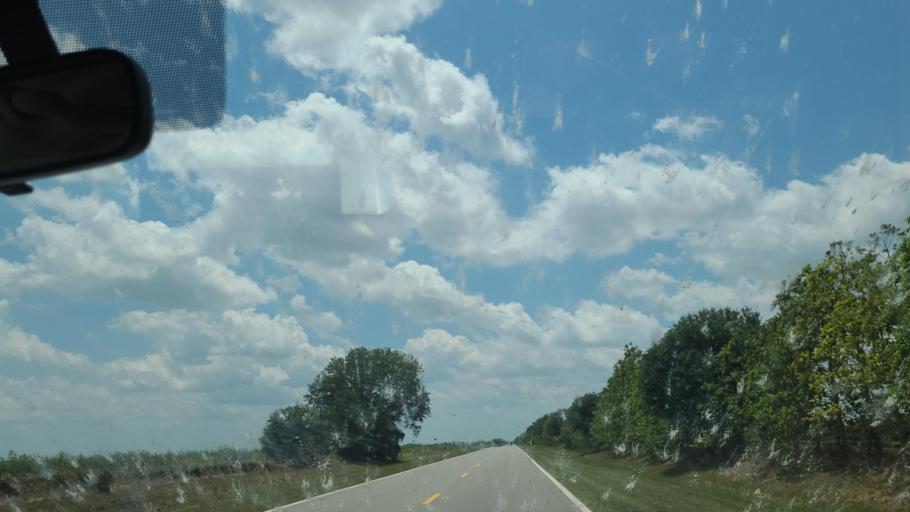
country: US
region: Florida
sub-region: Glades County
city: Buckhead Ridge
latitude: 27.2946
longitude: -81.0541
